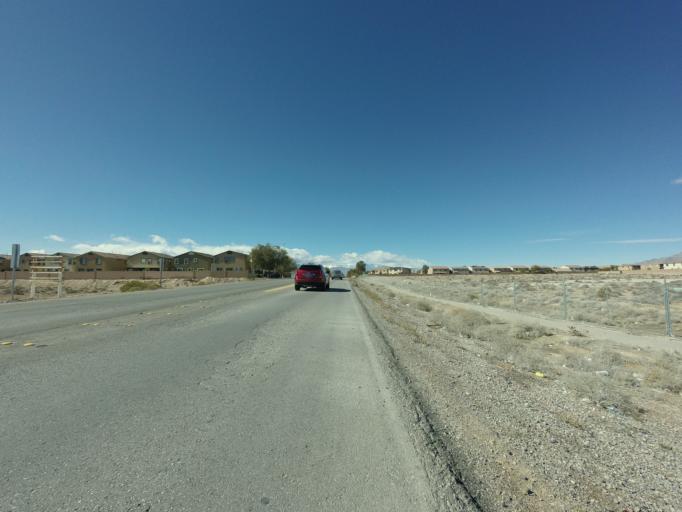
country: US
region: Nevada
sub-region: Clark County
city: Nellis Air Force Base
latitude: 36.2693
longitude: -115.0823
